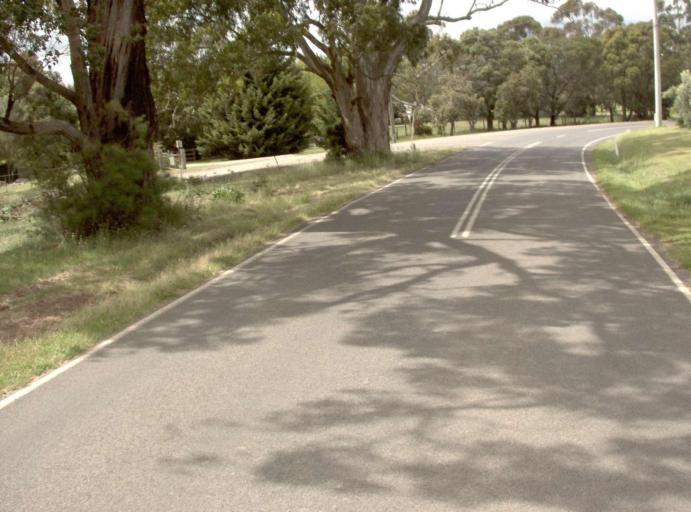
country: AU
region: Victoria
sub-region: Latrobe
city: Moe
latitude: -38.0297
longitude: 146.1652
